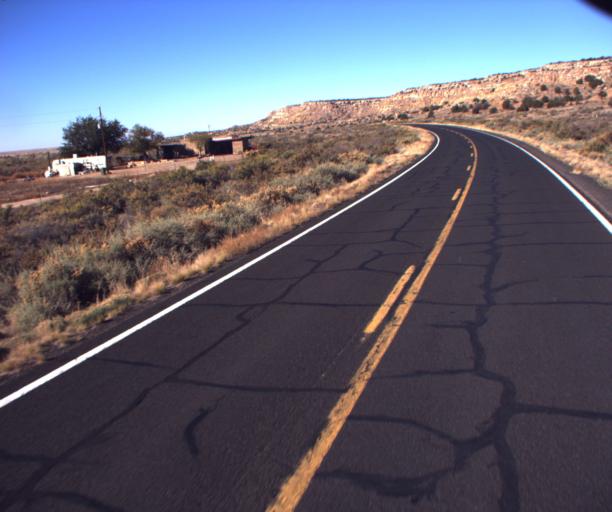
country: US
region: Arizona
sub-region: Navajo County
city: First Mesa
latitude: 35.8422
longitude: -110.2442
